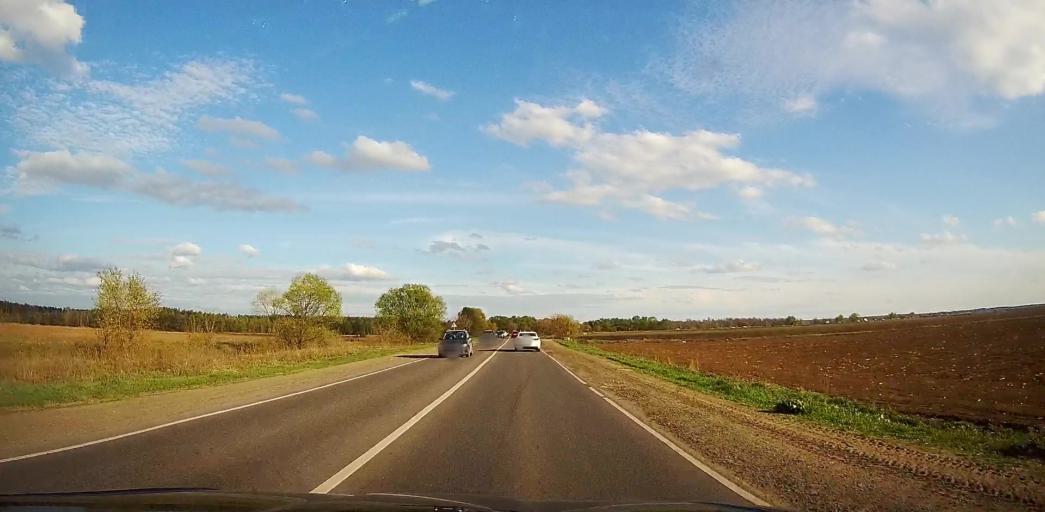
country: RU
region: Moskovskaya
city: Ramenskoye
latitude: 55.5338
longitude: 38.2786
